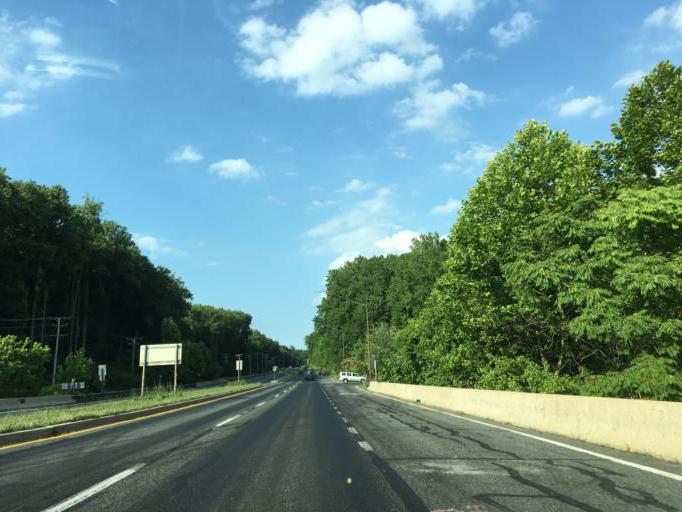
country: US
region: Maryland
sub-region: Baltimore County
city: Perry Hall
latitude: 39.4273
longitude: -76.4446
